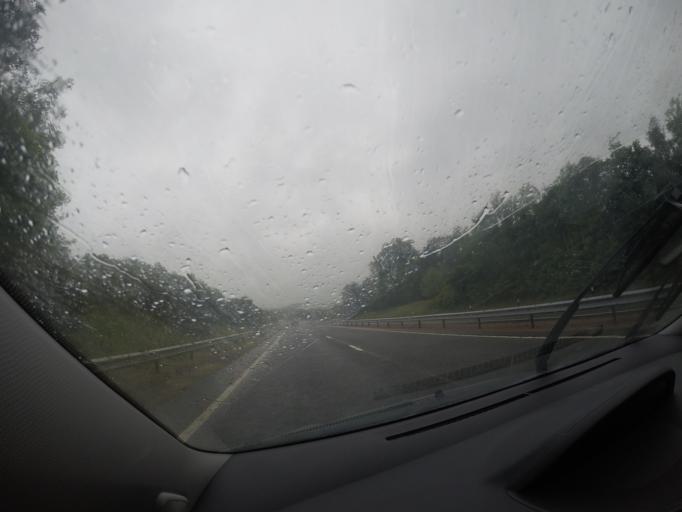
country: GB
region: Scotland
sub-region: Angus
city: Forfar
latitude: 56.5988
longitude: -2.9083
